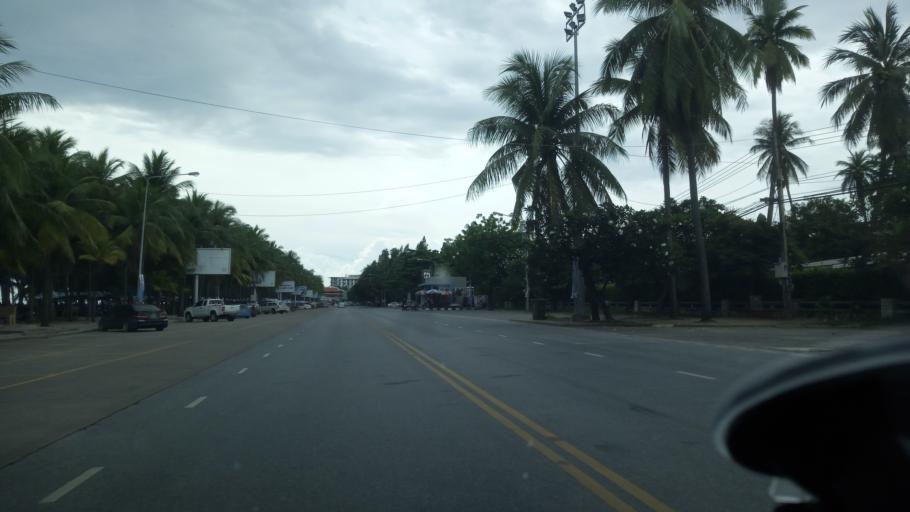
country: TH
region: Chon Buri
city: Chon Buri
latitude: 13.2955
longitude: 100.9055
